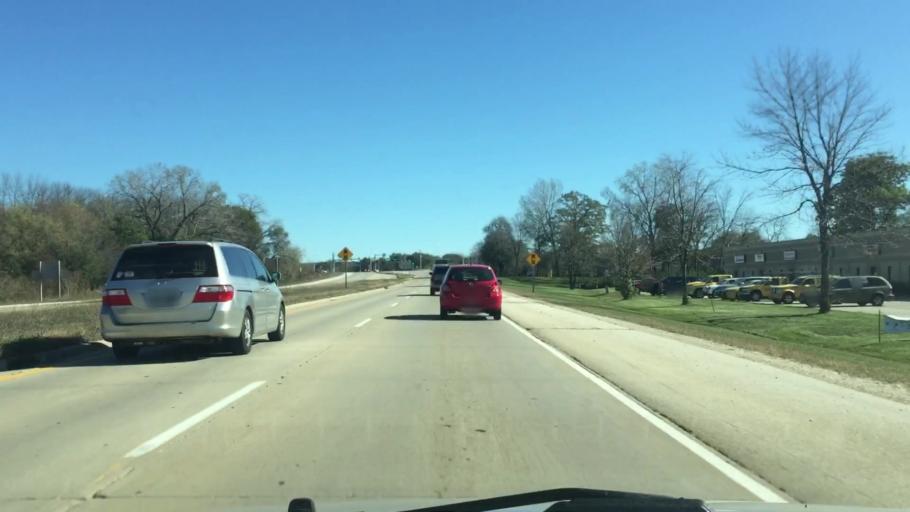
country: US
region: Wisconsin
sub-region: Waukesha County
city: Waukesha
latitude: 42.9770
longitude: -88.2330
